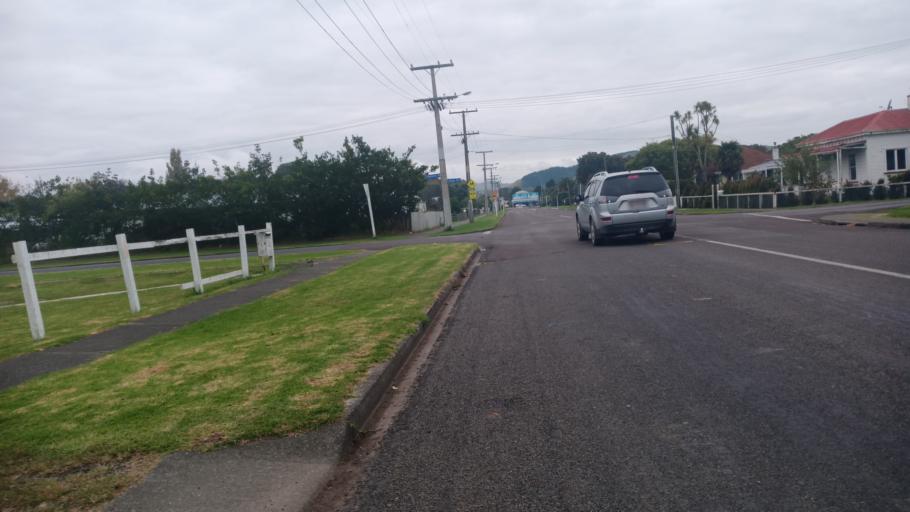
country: NZ
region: Gisborne
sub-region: Gisborne District
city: Gisborne
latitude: -38.6770
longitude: 178.0420
